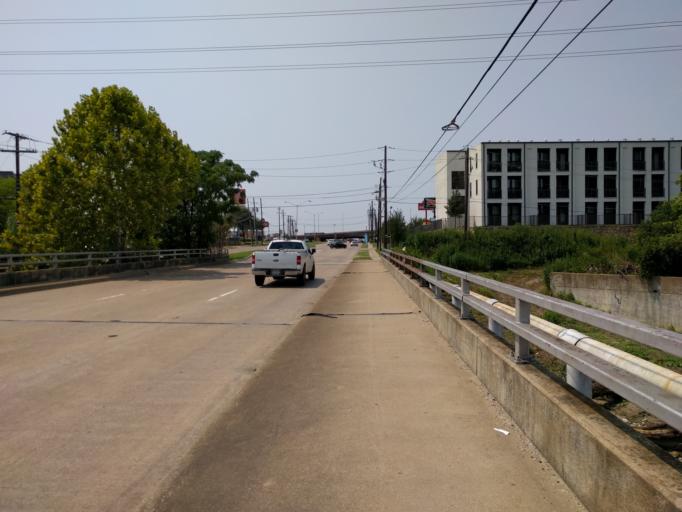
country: US
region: Texas
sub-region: Dallas County
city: Richardson
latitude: 32.9094
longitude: -96.7650
